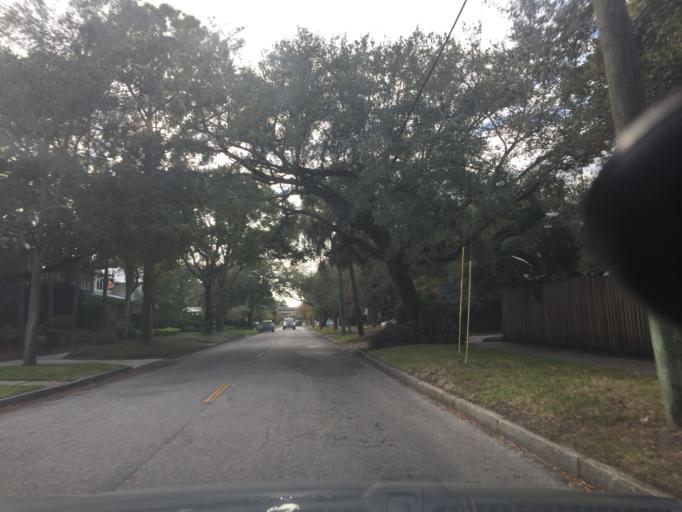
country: US
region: Florida
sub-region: Hillsborough County
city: Tampa
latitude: 27.9337
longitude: -82.4792
